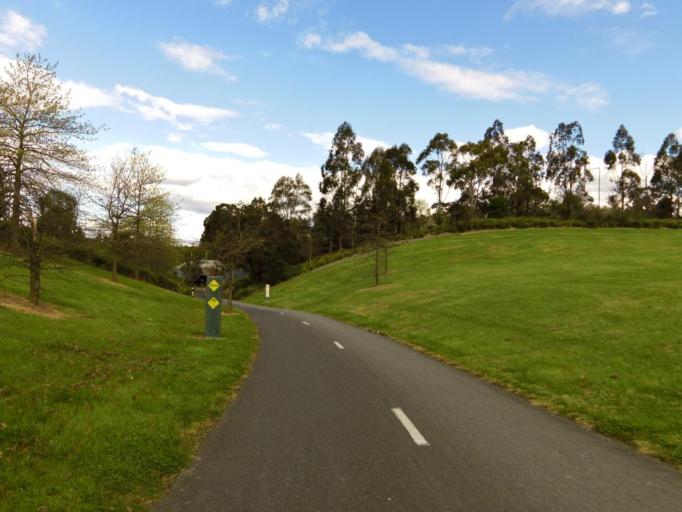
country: AU
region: Victoria
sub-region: Boroondara
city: Balwyn North
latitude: -37.7883
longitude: 145.1012
